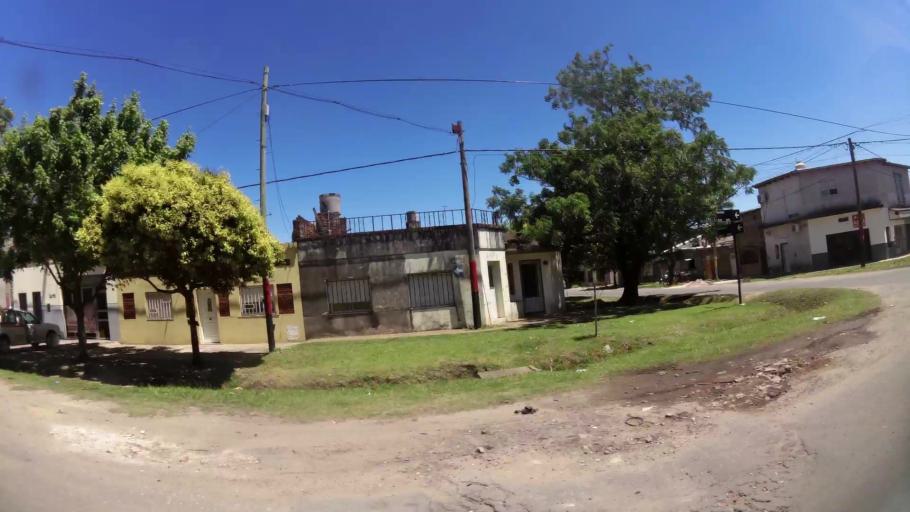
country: AR
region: Santa Fe
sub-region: Departamento de Rosario
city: Rosario
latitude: -32.9568
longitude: -60.7016
